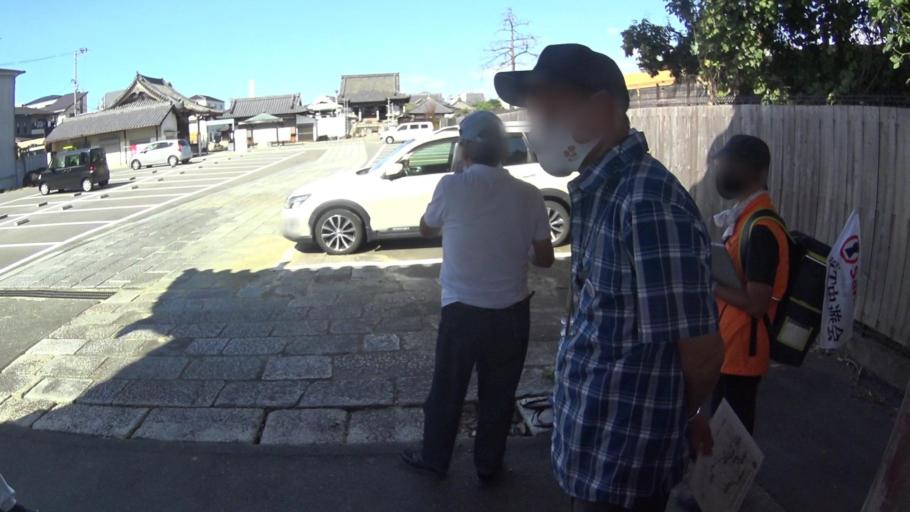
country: JP
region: Ehime
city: Kihoku-cho
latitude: 33.3807
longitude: 132.8211
